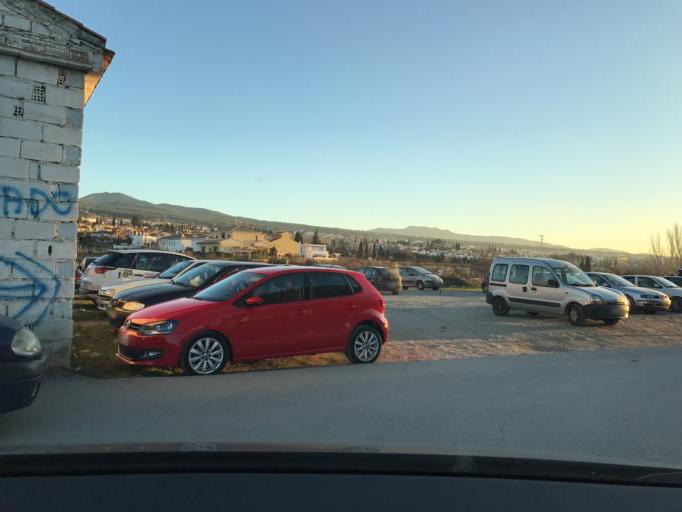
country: ES
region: Andalusia
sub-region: Provincia de Granada
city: Cajar
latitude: 37.1335
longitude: -3.5755
